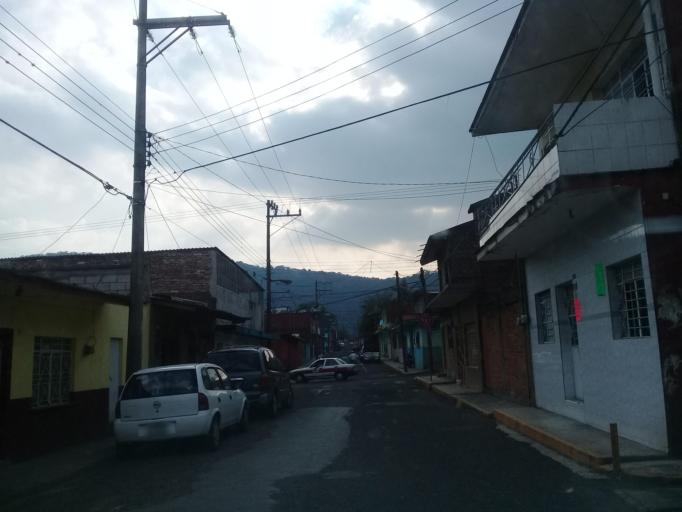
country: MX
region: Veracruz
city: Orizaba
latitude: 18.8595
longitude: -97.1055
